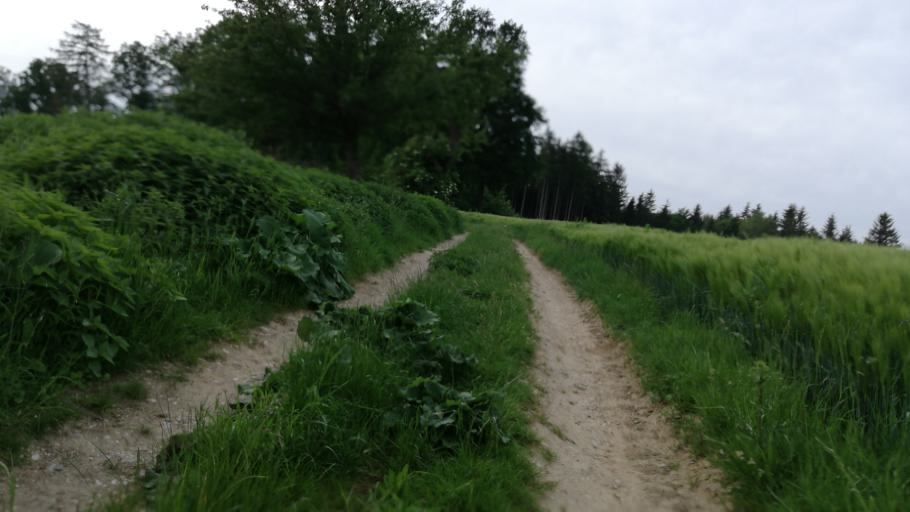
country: AT
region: Upper Austria
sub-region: Wels-Land
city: Gunskirchen
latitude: 48.1790
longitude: 13.9454
